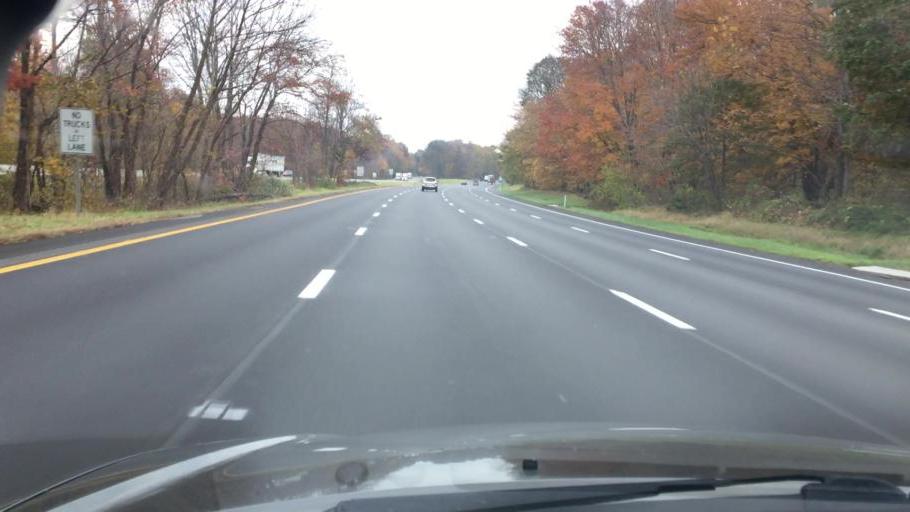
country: US
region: New Jersey
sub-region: Warren County
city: Belvidere
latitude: 40.9333
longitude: -75.0248
